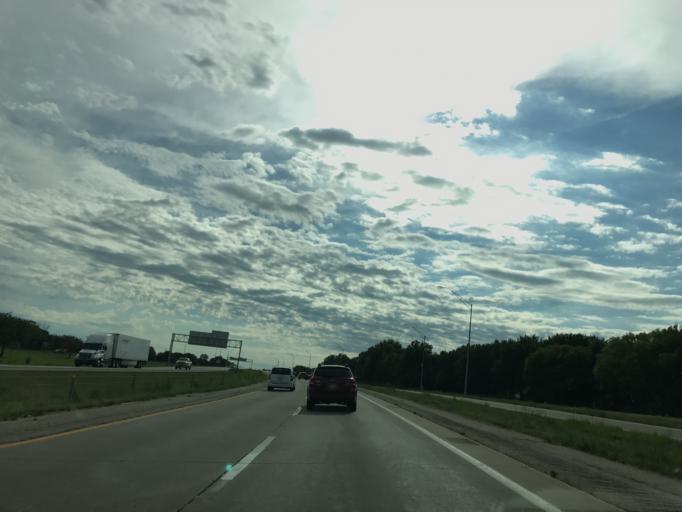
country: US
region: Iowa
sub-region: Dallas County
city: Waukee
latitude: 41.5916
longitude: -93.8101
